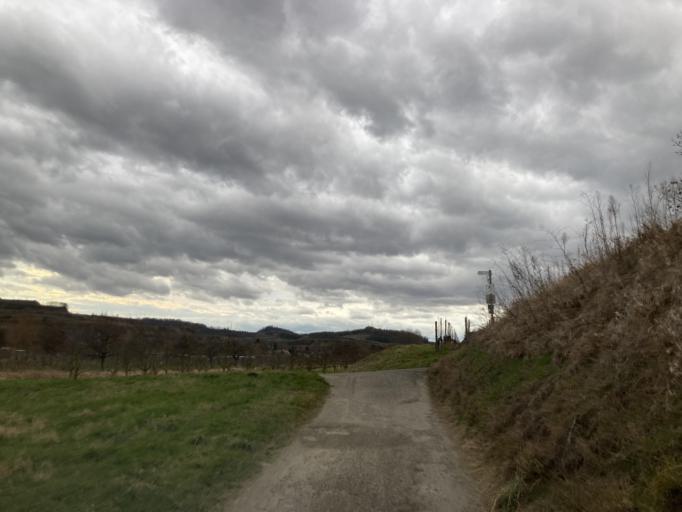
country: DE
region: Baden-Wuerttemberg
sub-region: Freiburg Region
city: Vogtsburg
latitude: 48.0950
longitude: 7.6480
